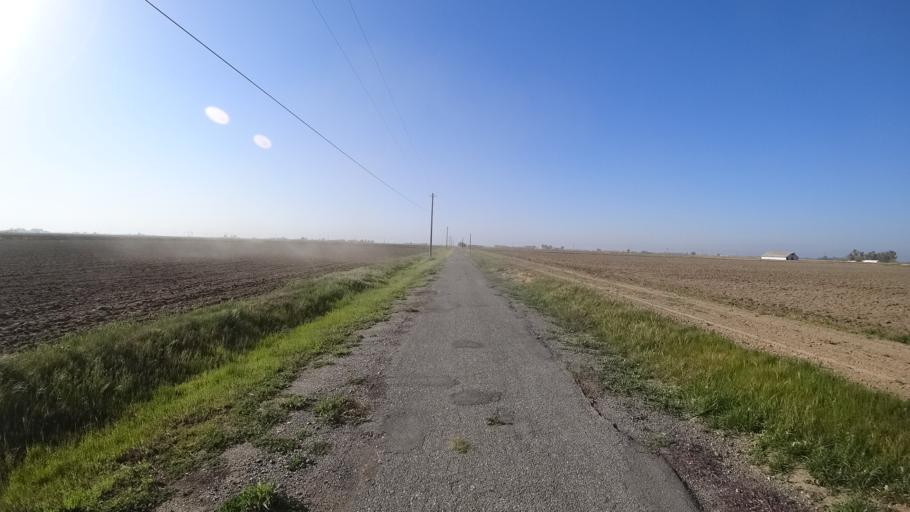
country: US
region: California
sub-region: Glenn County
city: Willows
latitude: 39.5584
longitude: -122.1321
